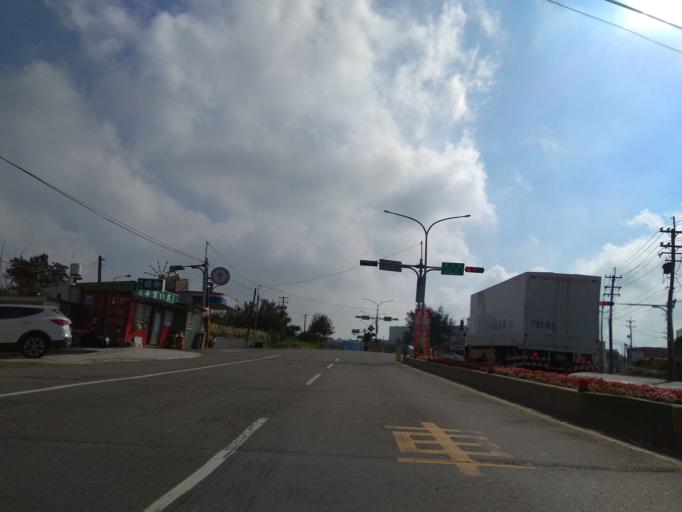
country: TW
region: Taiwan
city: Taoyuan City
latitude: 25.0367
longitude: 121.1032
